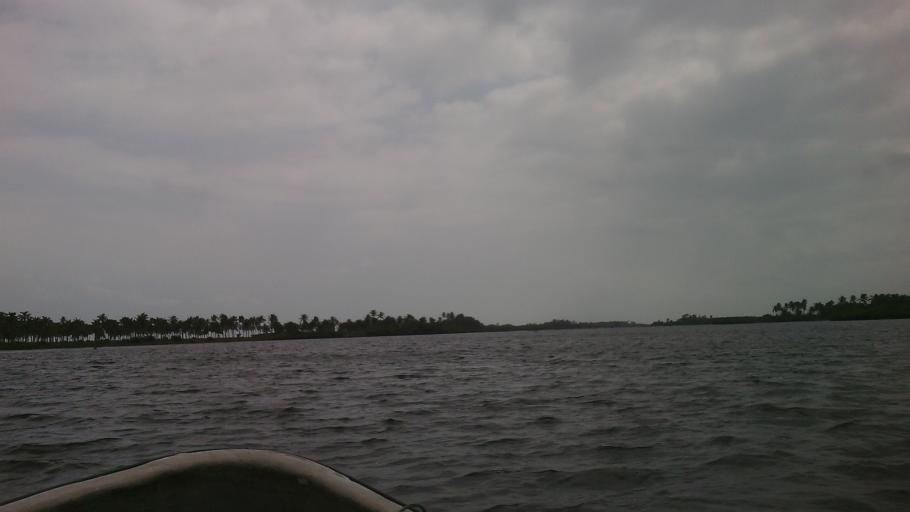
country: BJ
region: Atlantique
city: Ouidah
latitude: 6.3091
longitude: 1.9910
